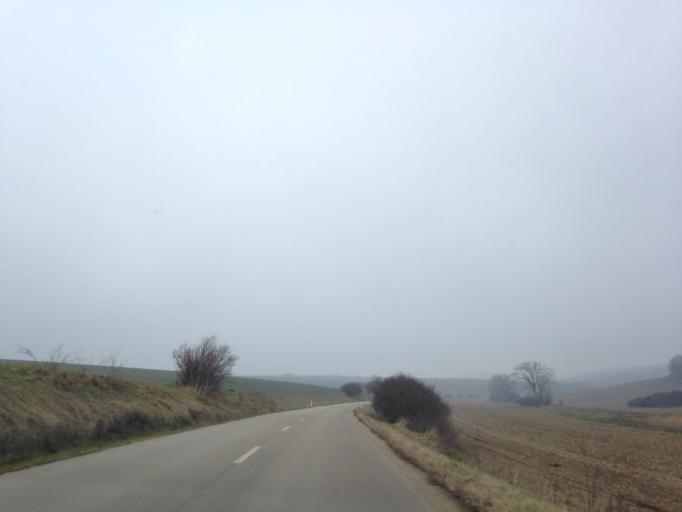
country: SK
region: Nitriansky
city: Svodin
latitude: 48.0154
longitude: 18.3638
